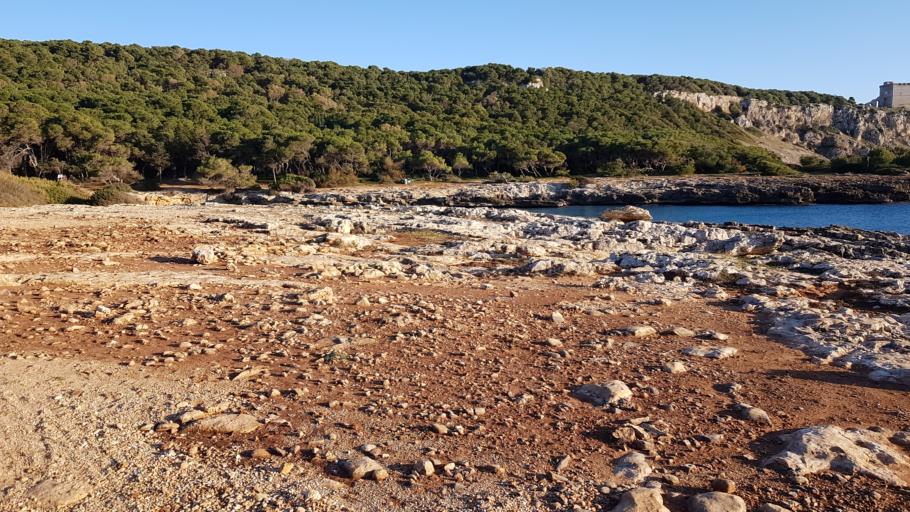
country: IT
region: Apulia
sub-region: Provincia di Lecce
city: Nardo
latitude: 40.1479
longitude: 17.9733
